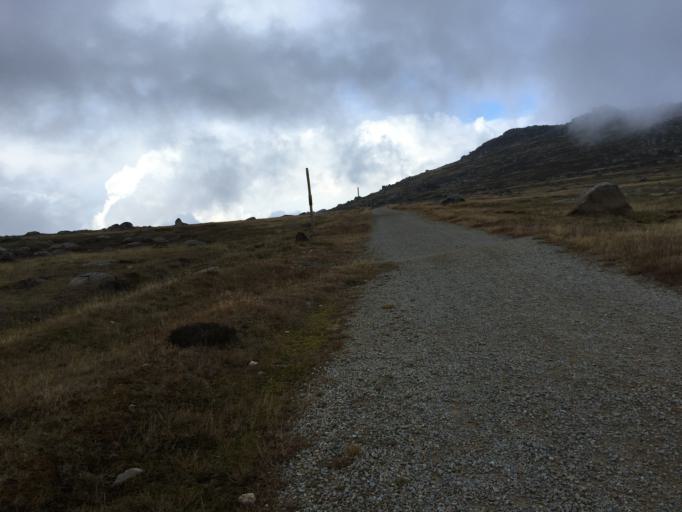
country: AU
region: New South Wales
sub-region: Snowy River
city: Jindabyne
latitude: -36.4579
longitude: 148.2982
